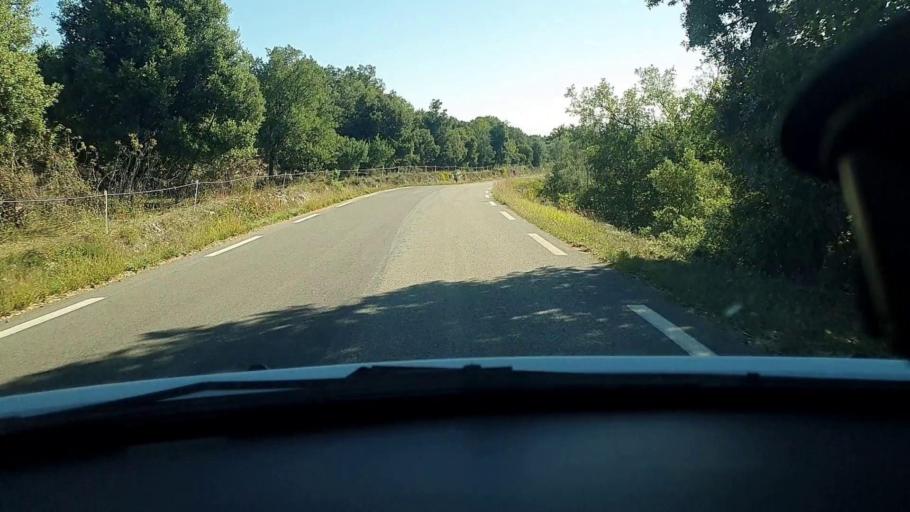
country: FR
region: Languedoc-Roussillon
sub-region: Departement du Gard
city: Goudargues
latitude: 44.2920
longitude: 4.4753
